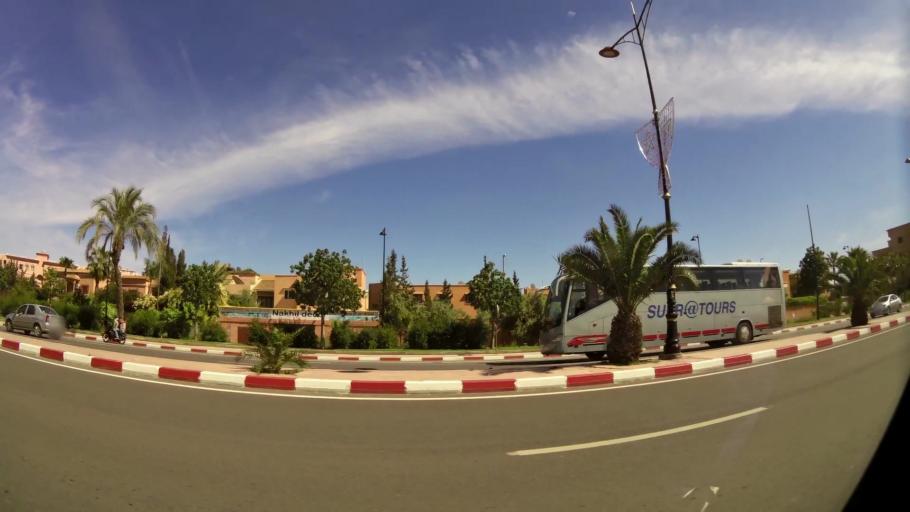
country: MA
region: Marrakech-Tensift-Al Haouz
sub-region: Marrakech
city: Marrakesh
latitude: 31.6723
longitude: -8.0064
